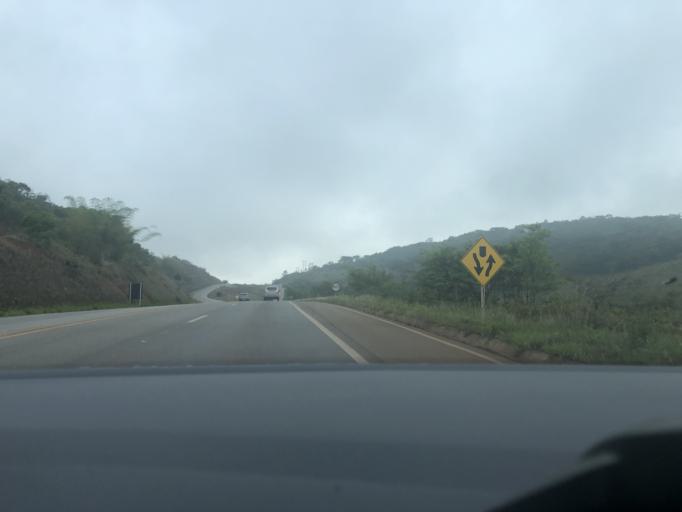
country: BR
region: Minas Gerais
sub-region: Congonhas
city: Congonhas
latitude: -20.5961
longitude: -43.9394
